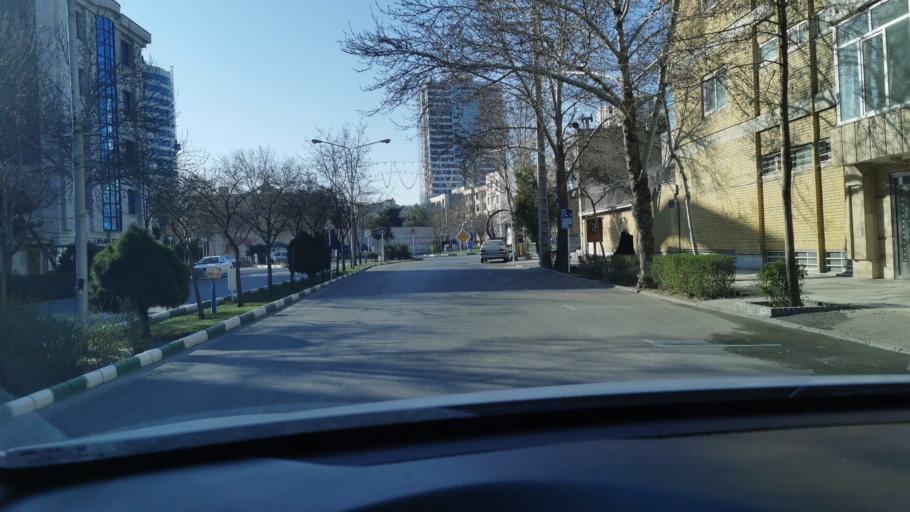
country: IR
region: Razavi Khorasan
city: Mashhad
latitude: 36.2872
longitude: 59.5673
